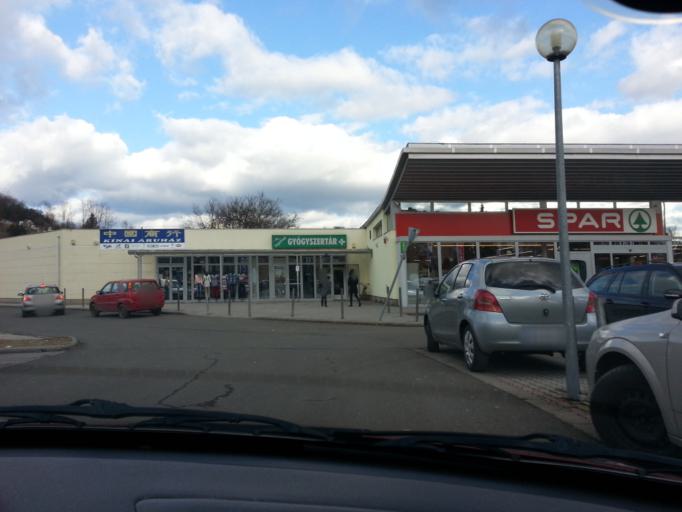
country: HU
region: Nograd
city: Salgotarjan
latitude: 48.0754
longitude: 19.7846
